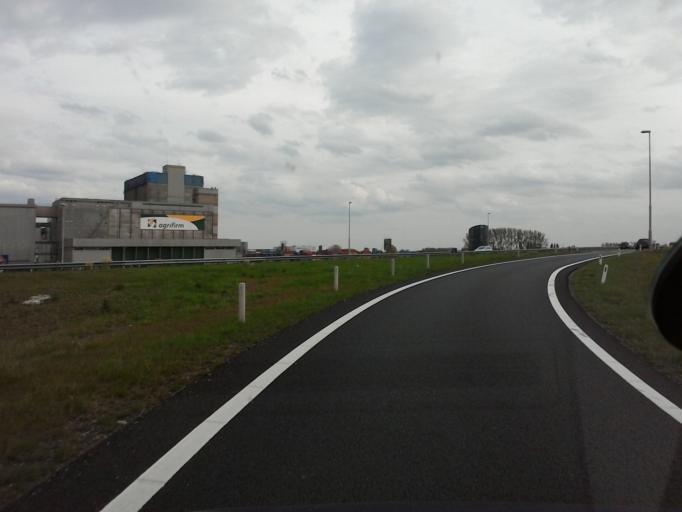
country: NL
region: North Brabant
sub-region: Gemeente Veghel
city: Eerde
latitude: 51.6255
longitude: 5.5041
